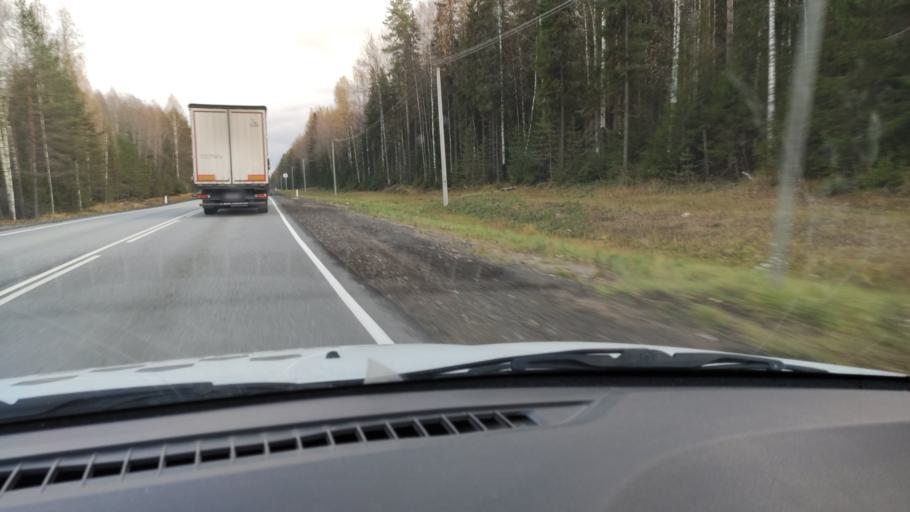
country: RU
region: Kirov
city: Dubrovka
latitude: 58.9122
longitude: 51.1695
